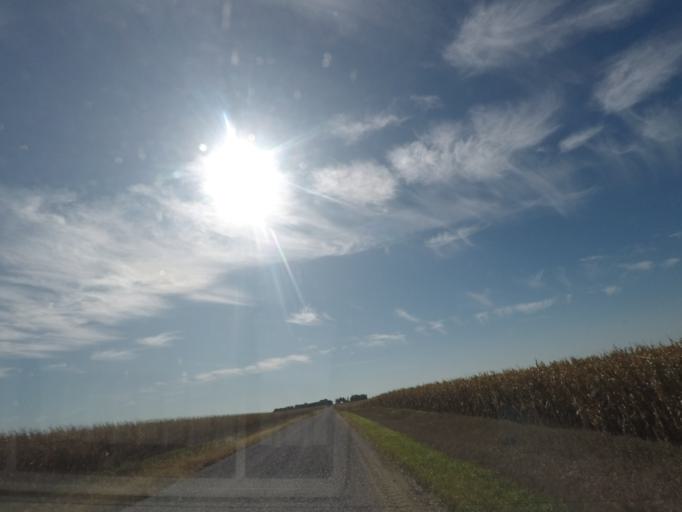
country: US
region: Iowa
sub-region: Story County
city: Nevada
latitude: 42.0607
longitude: -93.3291
